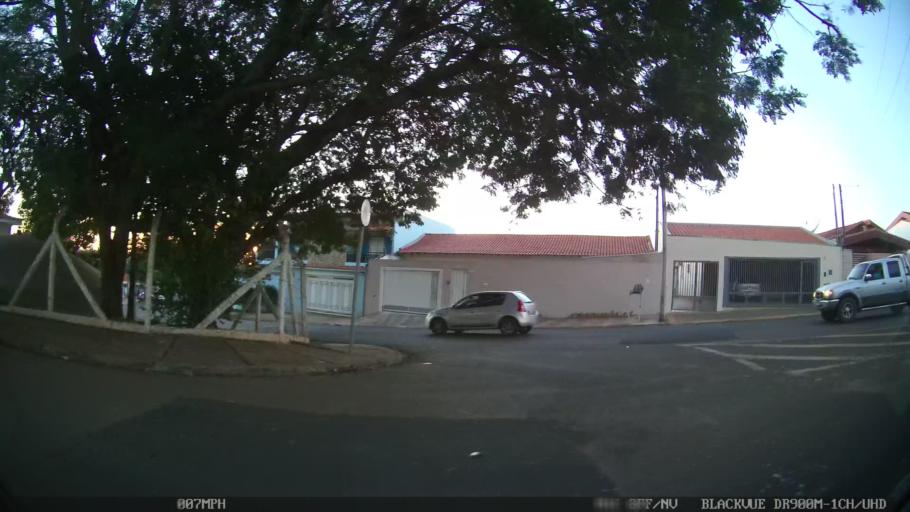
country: BR
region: Sao Paulo
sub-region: Santa Barbara D'Oeste
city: Santa Barbara d'Oeste
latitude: -22.7597
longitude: -47.4028
